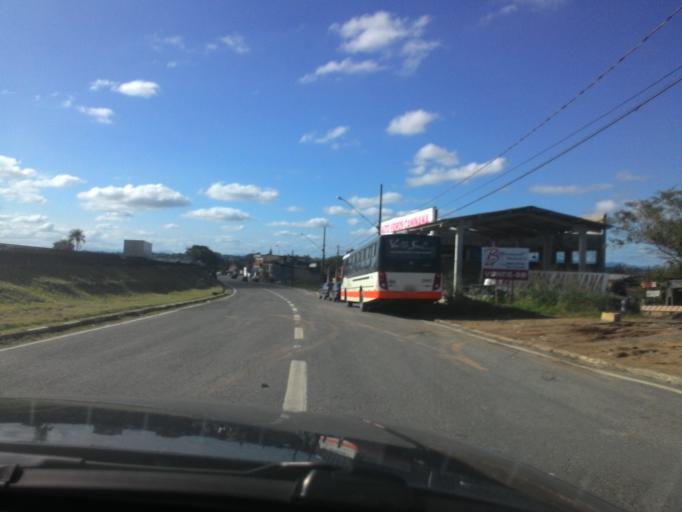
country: BR
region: Sao Paulo
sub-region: Registro
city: Registro
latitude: -24.4935
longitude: -47.8373
